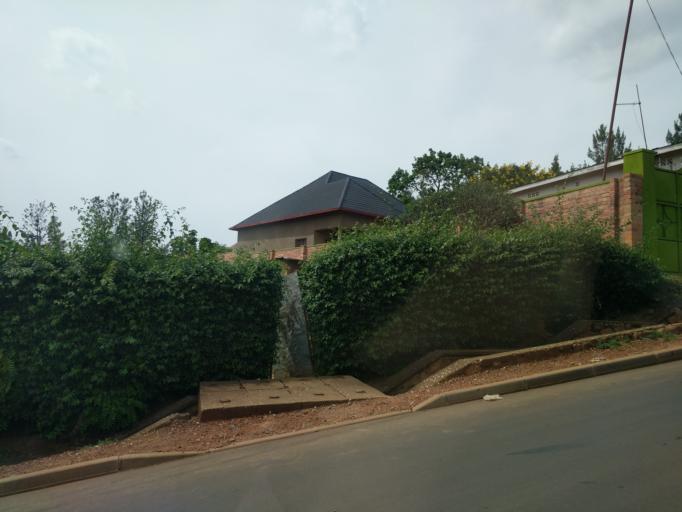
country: RW
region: Kigali
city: Kigali
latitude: -1.9733
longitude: 30.1214
